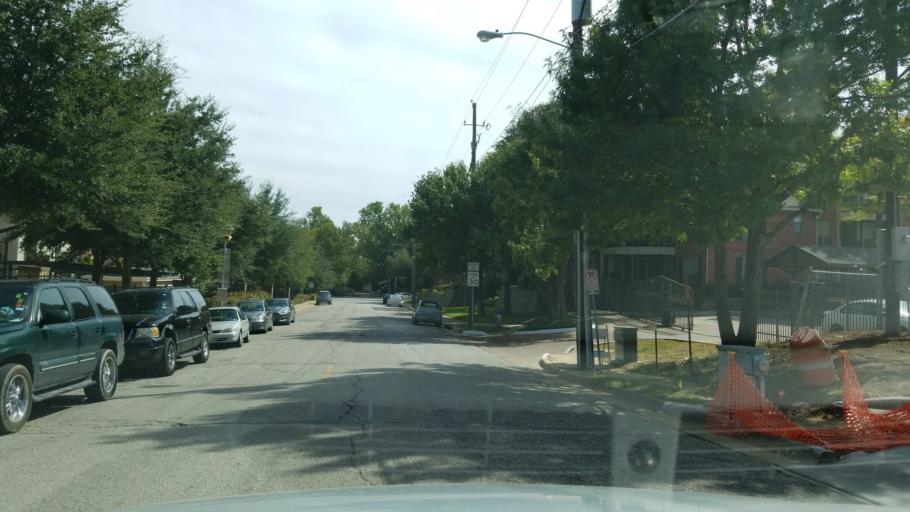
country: US
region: Texas
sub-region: Dallas County
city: Highland Park
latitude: 32.8065
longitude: -96.7306
